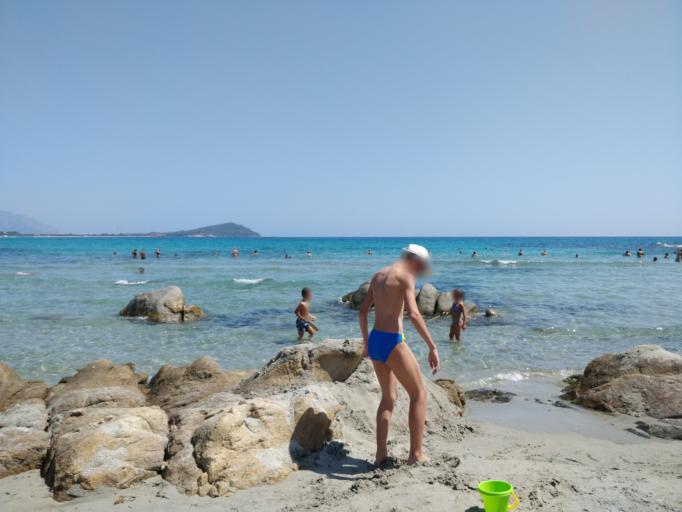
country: IT
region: Sardinia
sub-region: Provincia di Ogliastra
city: Tortoli
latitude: 39.8808
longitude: 9.6820
